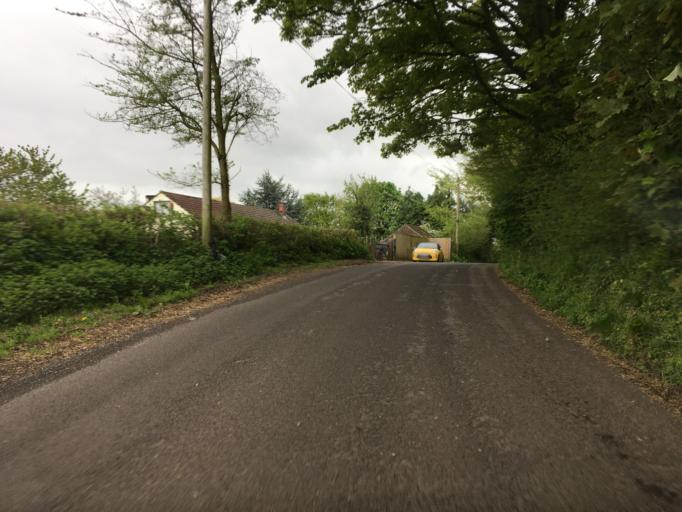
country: GB
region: England
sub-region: Bath and North East Somerset
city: Clutton
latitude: 51.3416
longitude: -2.5394
